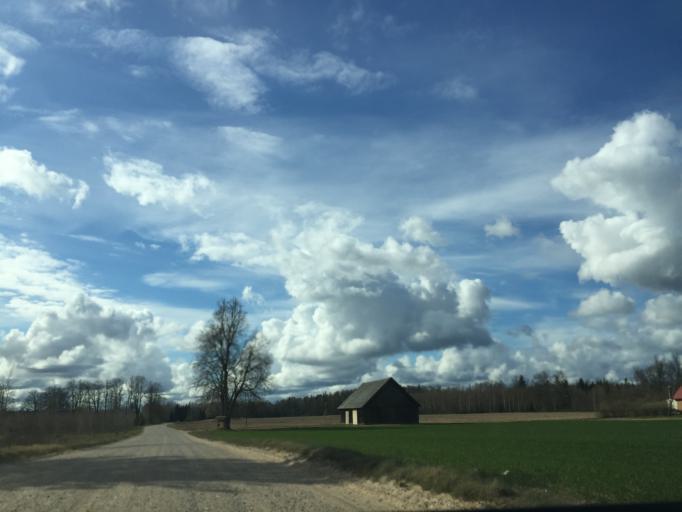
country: LV
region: Burtnieki
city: Matisi
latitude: 57.5993
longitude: 25.0675
